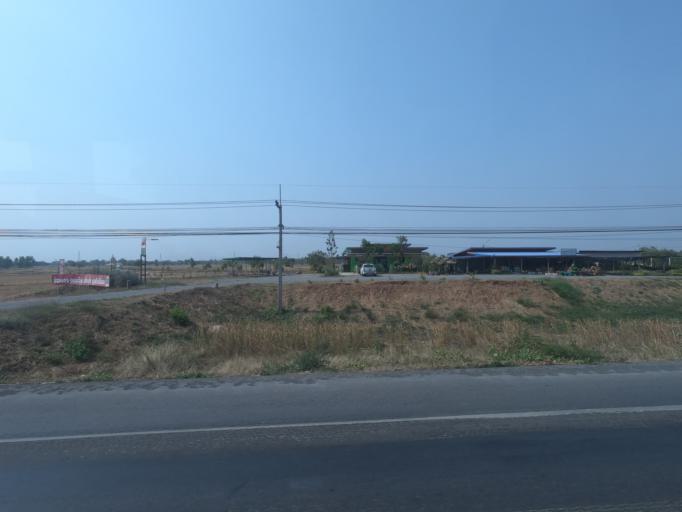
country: TH
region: Nakhon Ratchasima
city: Phimai
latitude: 15.3053
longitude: 102.4233
